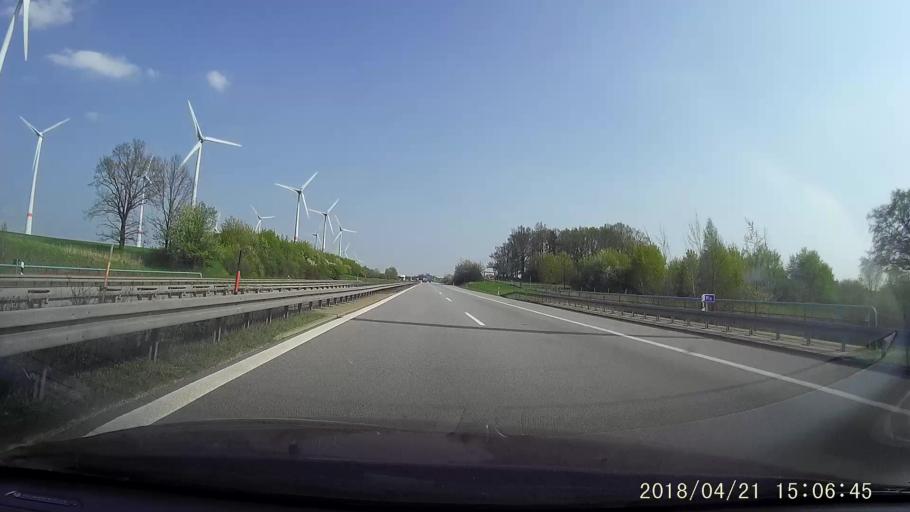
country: DE
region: Saxony
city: Kodersdorf
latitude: 51.2085
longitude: 14.9440
